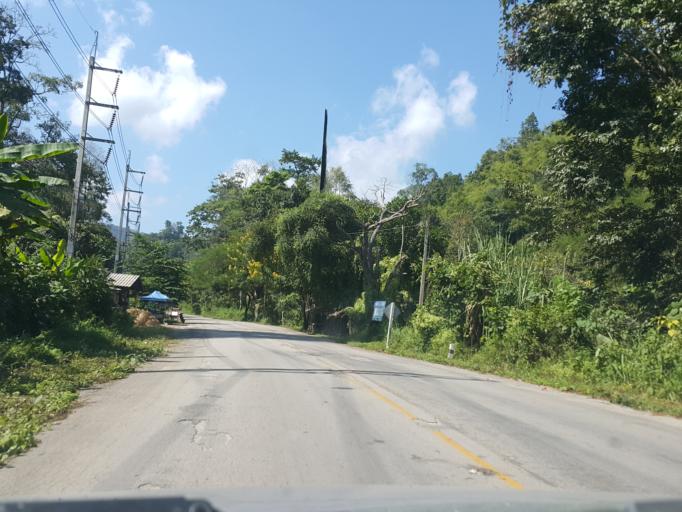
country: TH
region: Chiang Mai
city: Mae Taeng
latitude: 19.1264
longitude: 98.7588
